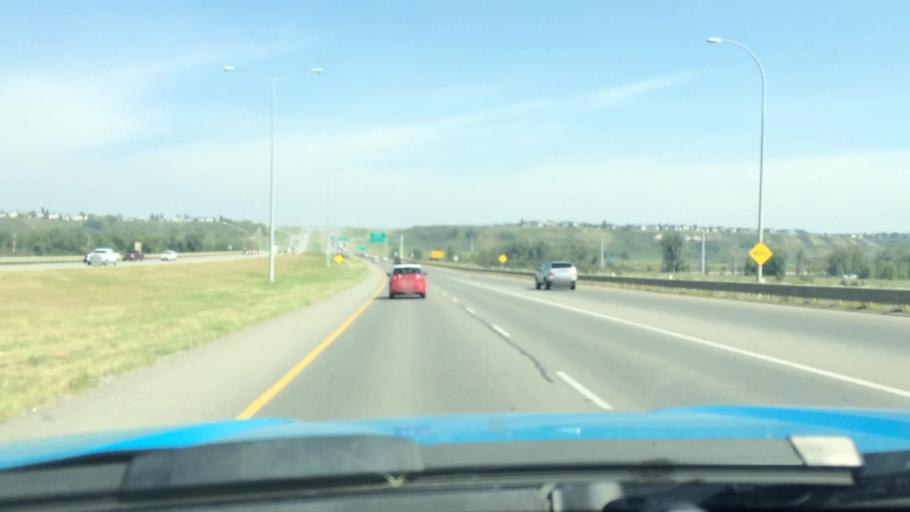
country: CA
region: Alberta
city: Okotoks
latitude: 50.8929
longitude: -114.0165
